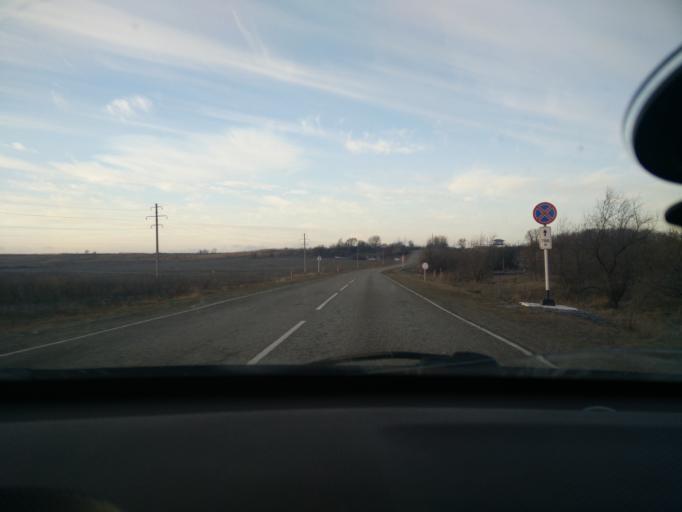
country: RU
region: Stavropol'skiy
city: Balakhonovskoye
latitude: 44.9834
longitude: 41.6958
